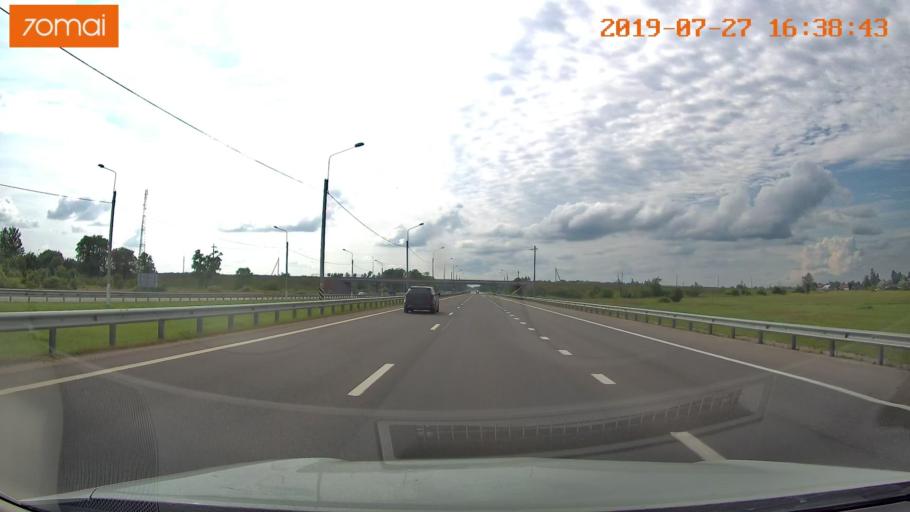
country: RU
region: Kaliningrad
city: Gvardeysk
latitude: 54.6491
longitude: 21.2205
